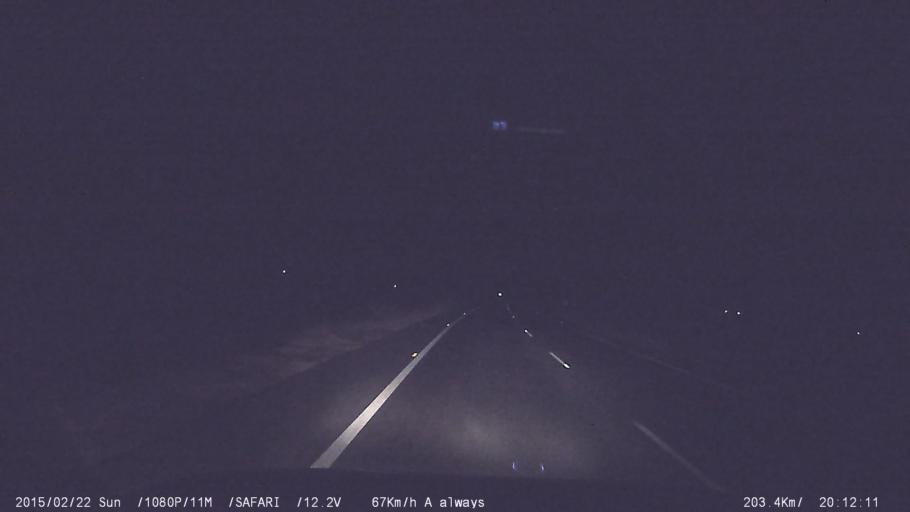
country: IN
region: Tamil Nadu
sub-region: Dindigul
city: Nilakottai
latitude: 10.2359
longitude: 77.8178
